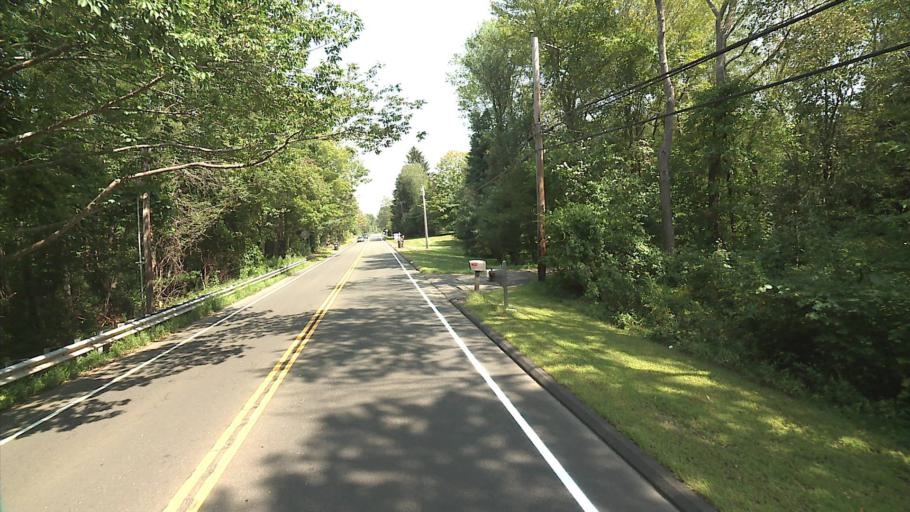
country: US
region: Connecticut
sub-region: Middlesex County
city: Durham
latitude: 41.4147
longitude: -72.6571
